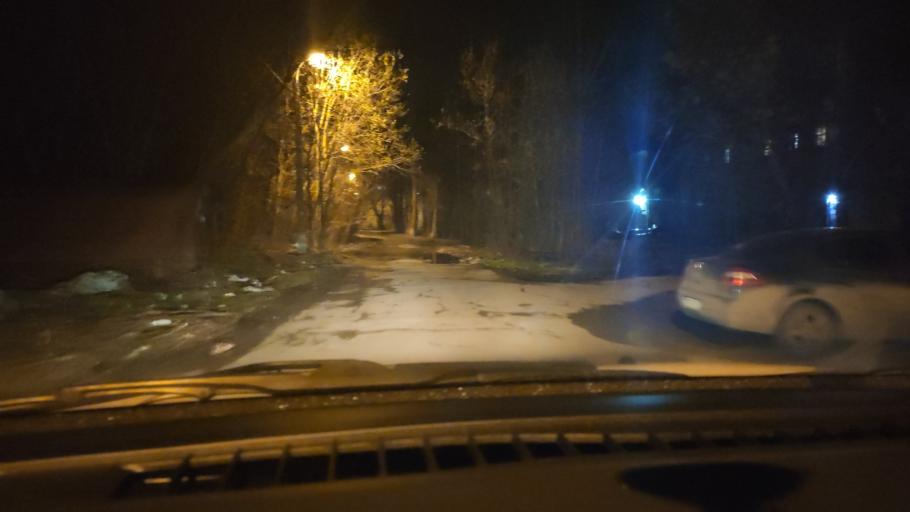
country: RU
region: Perm
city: Perm
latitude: 58.0878
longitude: 56.3866
